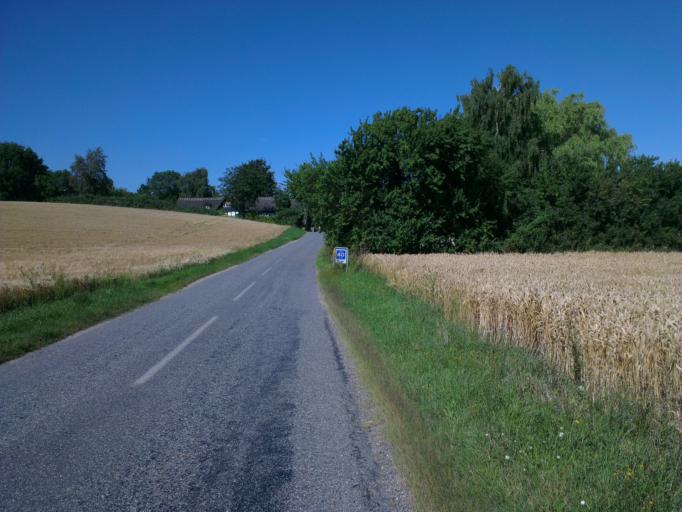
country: DK
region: Capital Region
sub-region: Frederikssund Kommune
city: Skibby
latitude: 55.7117
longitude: 11.9492
